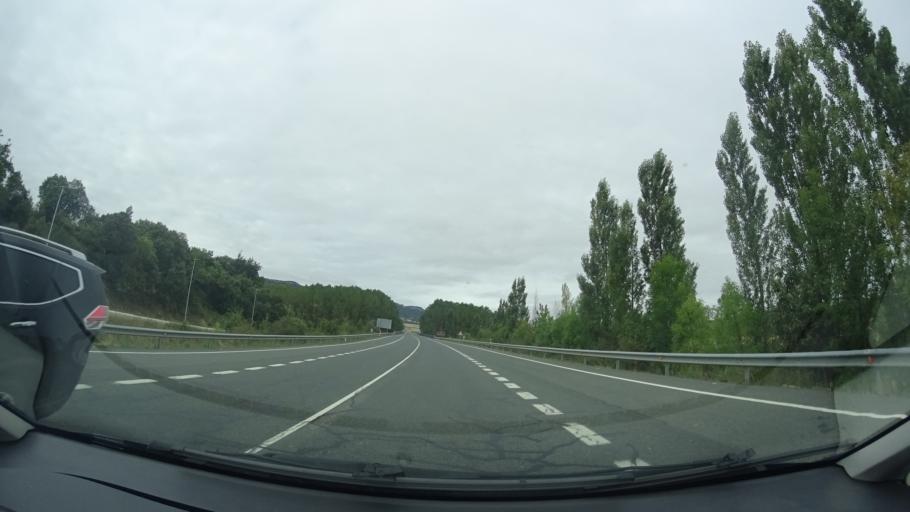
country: ES
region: Basque Country
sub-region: Provincia de Alava
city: Arminon
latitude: 42.8130
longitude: -2.8101
